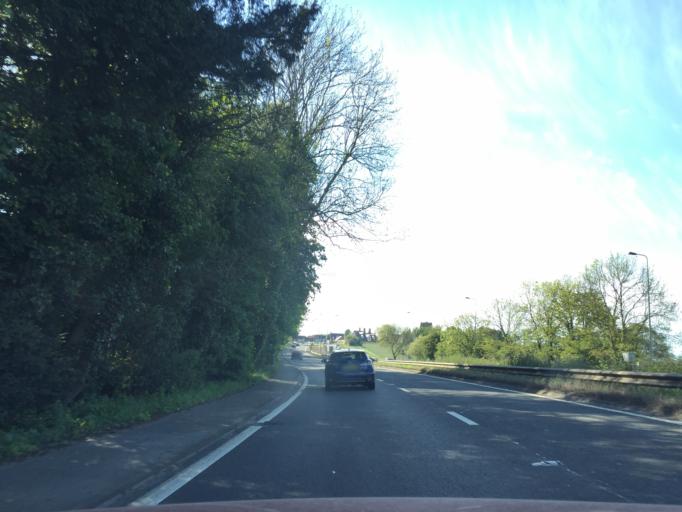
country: GB
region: England
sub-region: Warwickshire
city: Ryton on Dunsmore
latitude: 52.3651
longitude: -1.4291
